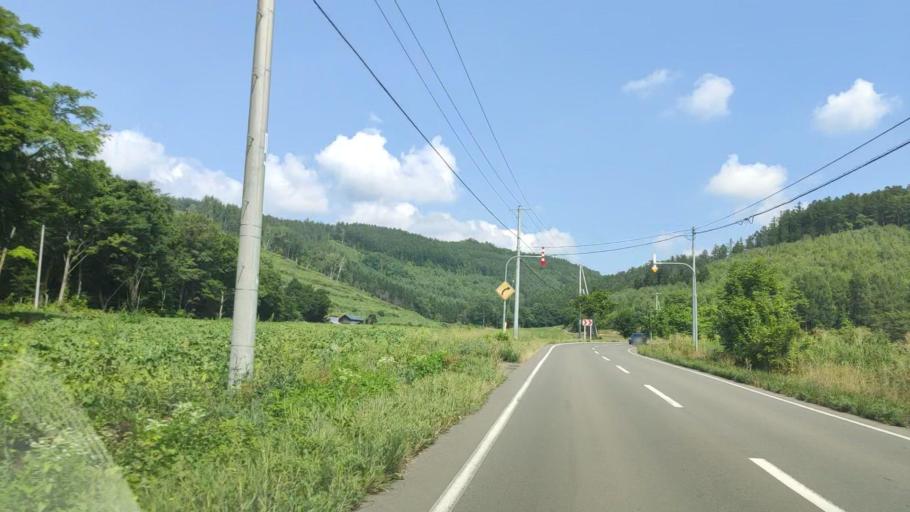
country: JP
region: Hokkaido
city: Shimo-furano
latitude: 43.4242
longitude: 142.4002
